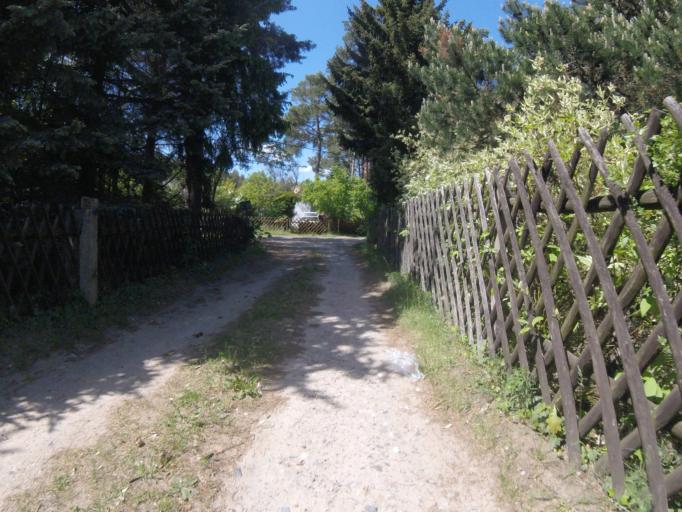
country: DE
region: Brandenburg
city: Teupitz
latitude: 52.1415
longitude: 13.5880
